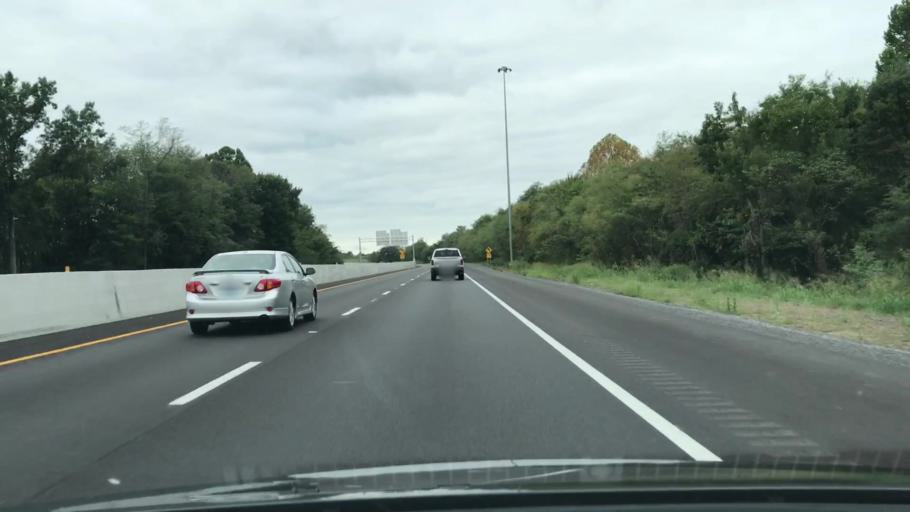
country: US
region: Kentucky
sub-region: Graves County
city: Mayfield
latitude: 36.7264
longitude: -88.6716
